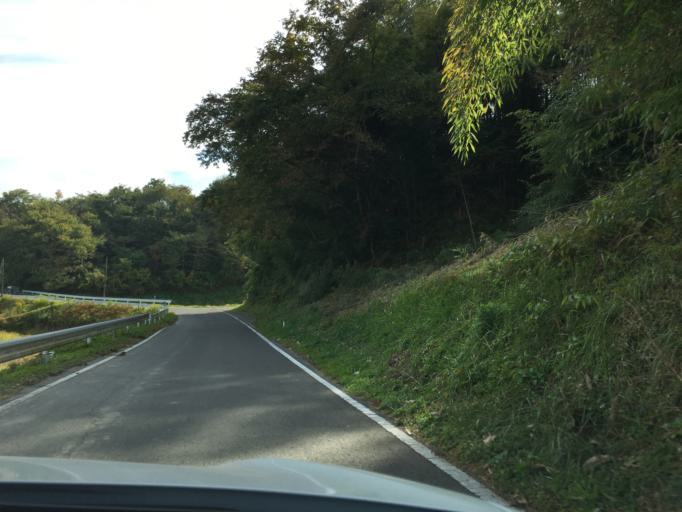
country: JP
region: Fukushima
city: Miharu
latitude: 37.5104
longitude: 140.4989
